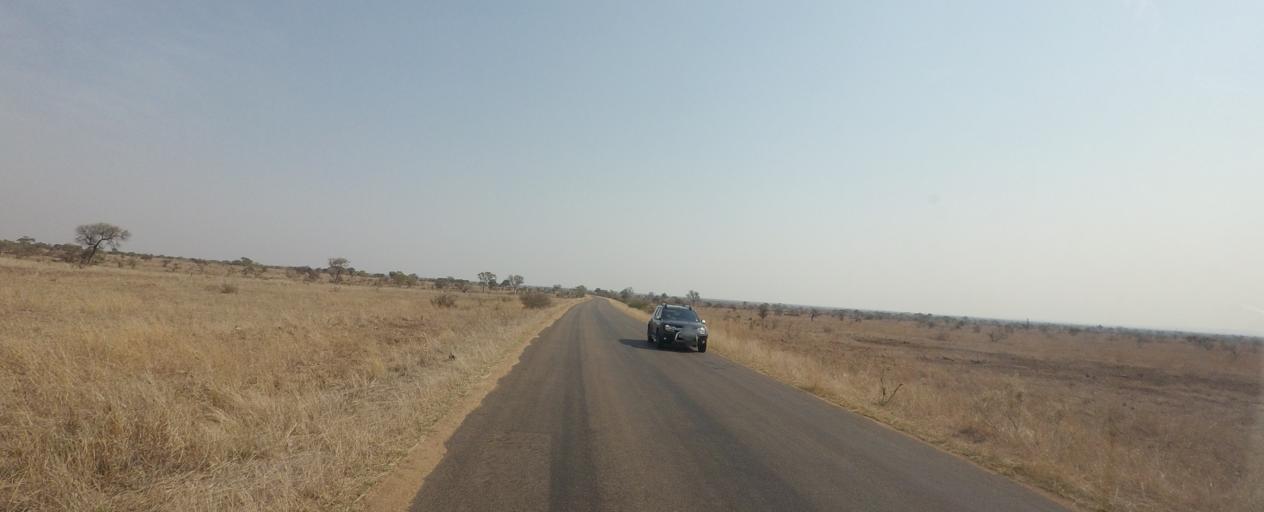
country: ZA
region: Limpopo
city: Thulamahashi
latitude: -24.3169
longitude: 31.7490
